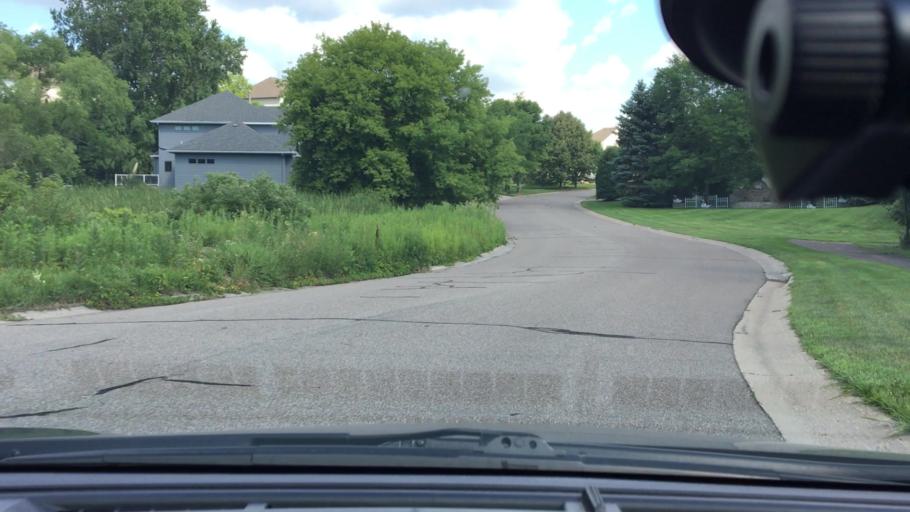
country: US
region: Minnesota
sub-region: Hennepin County
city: Plymouth
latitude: 45.0325
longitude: -93.4453
